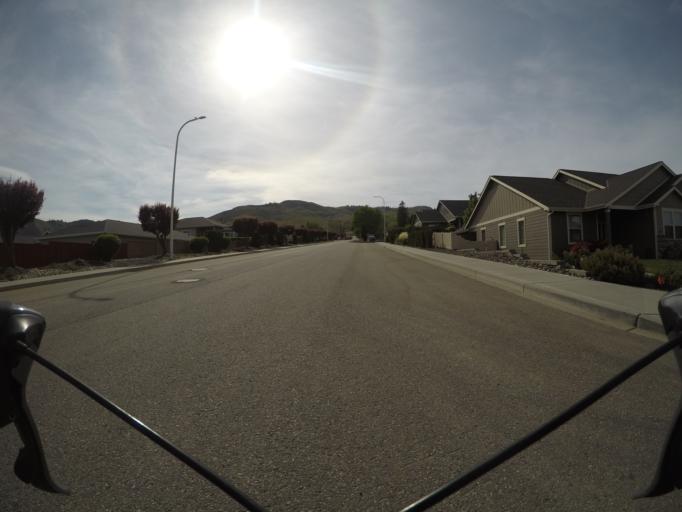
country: US
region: Washington
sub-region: Chelan County
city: West Wenatchee
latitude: 47.4426
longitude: -120.3494
